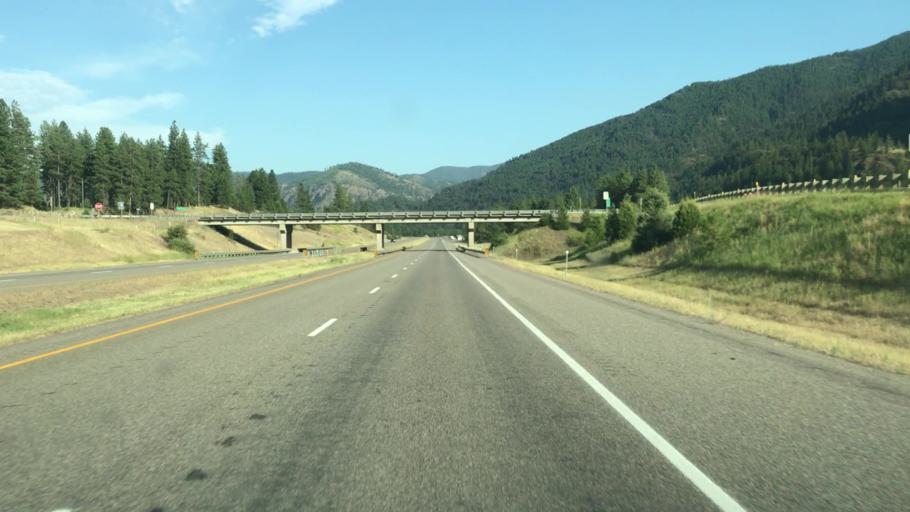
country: US
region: Montana
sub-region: Missoula County
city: Frenchtown
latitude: 47.0067
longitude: -114.4956
